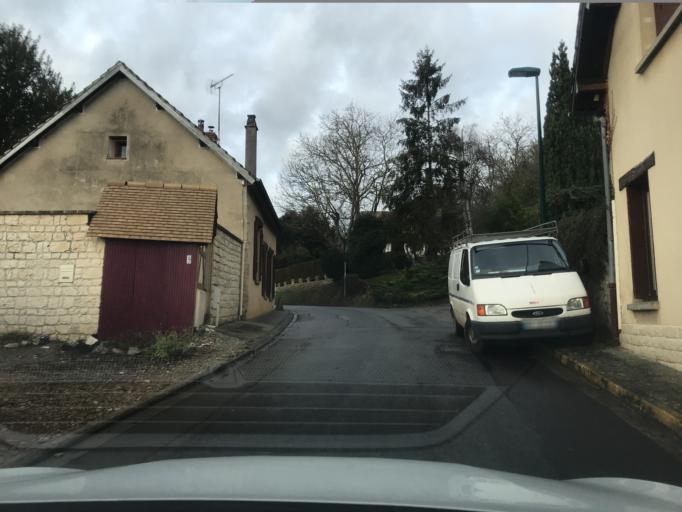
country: FR
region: Haute-Normandie
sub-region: Departement de l'Eure
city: Gasny
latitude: 49.0839
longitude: 1.5847
